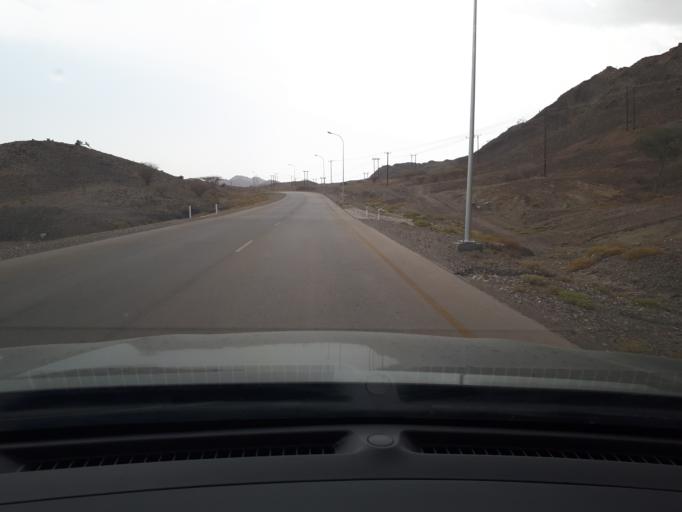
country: OM
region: Ash Sharqiyah
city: Badiyah
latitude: 22.5587
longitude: 59.0200
